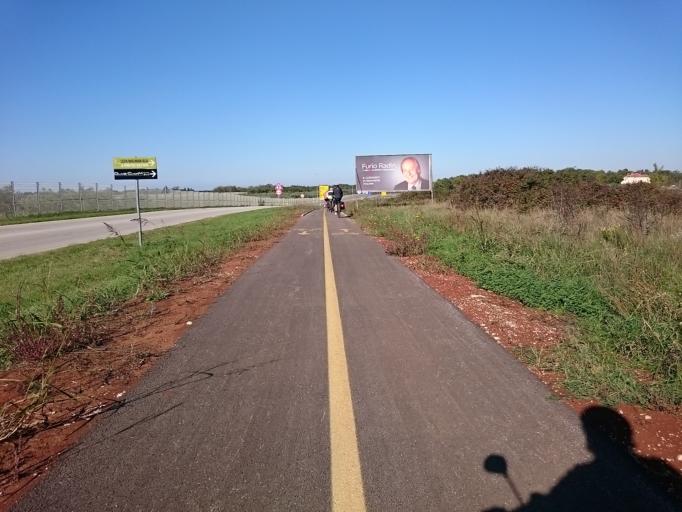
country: HR
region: Istarska
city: Umag
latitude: 45.4114
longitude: 13.5304
